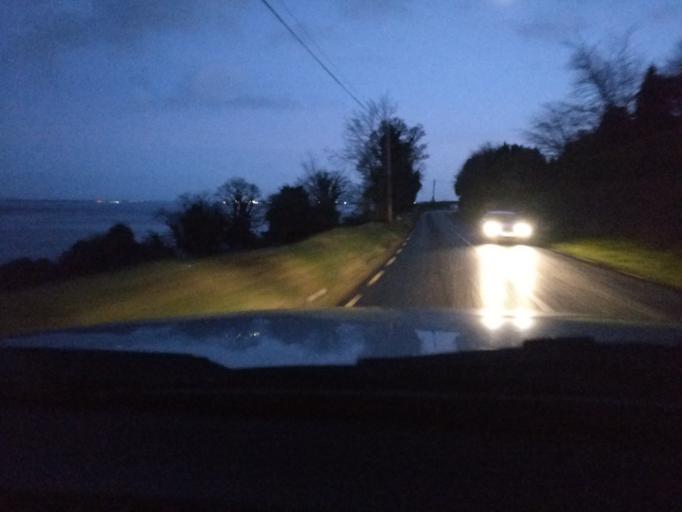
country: IE
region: Leinster
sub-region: Lu
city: Carlingford
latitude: 54.0556
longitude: -6.1972
